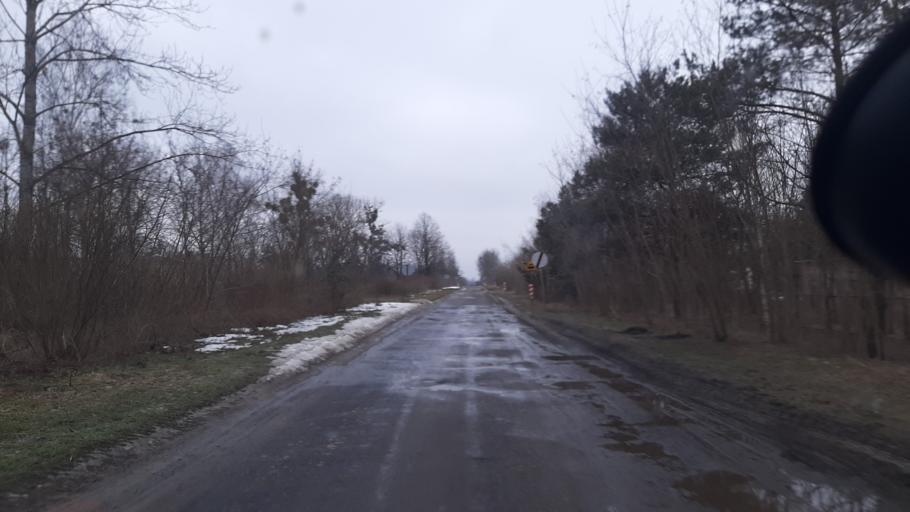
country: PL
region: Lublin Voivodeship
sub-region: Powiat wlodawski
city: Wlodawa
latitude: 51.5185
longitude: 23.5912
